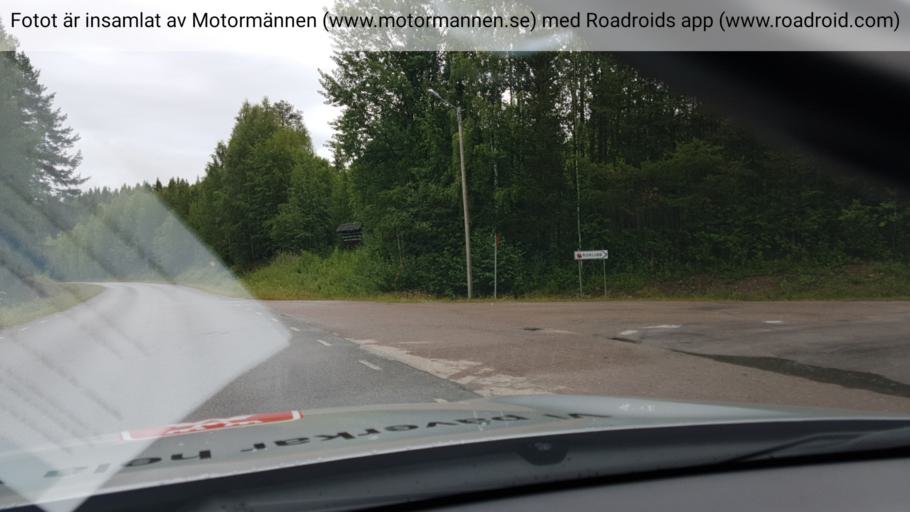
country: SE
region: Norrbotten
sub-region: Gallivare Kommun
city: Gaellivare
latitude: 66.4440
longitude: 20.6490
